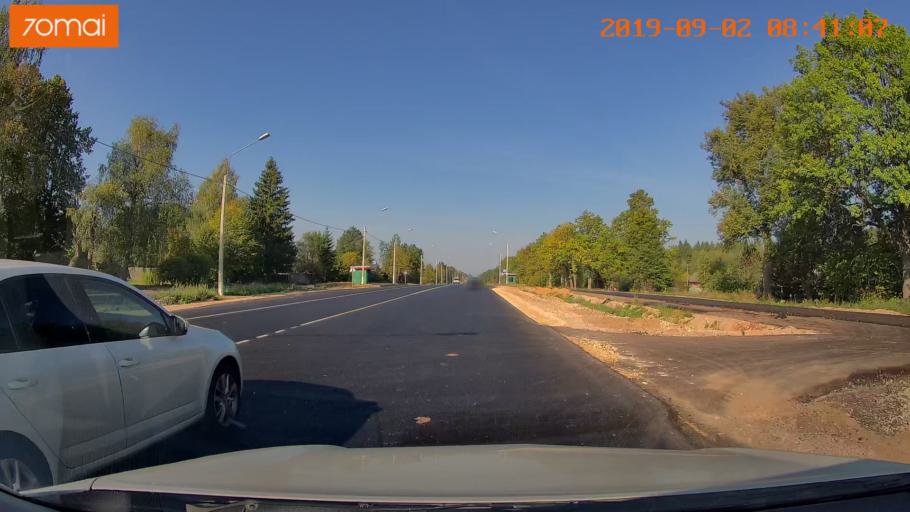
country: RU
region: Kaluga
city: Kudinovo
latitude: 54.9735
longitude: 36.1181
